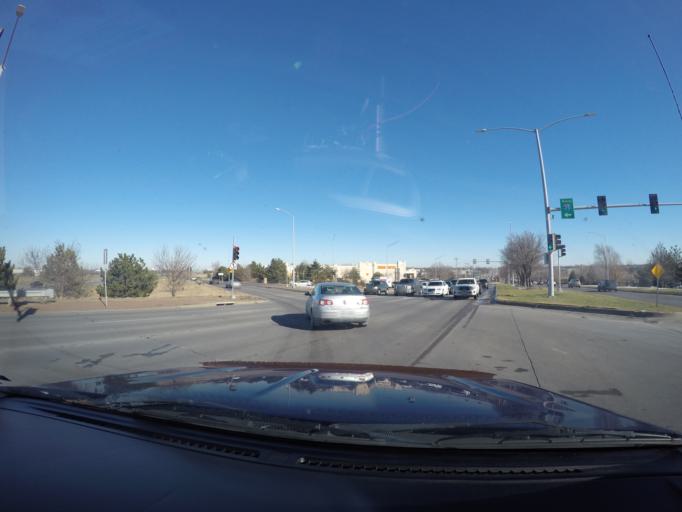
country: US
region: Kansas
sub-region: Johnson County
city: Lenexa
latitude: 38.9128
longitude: -94.7701
